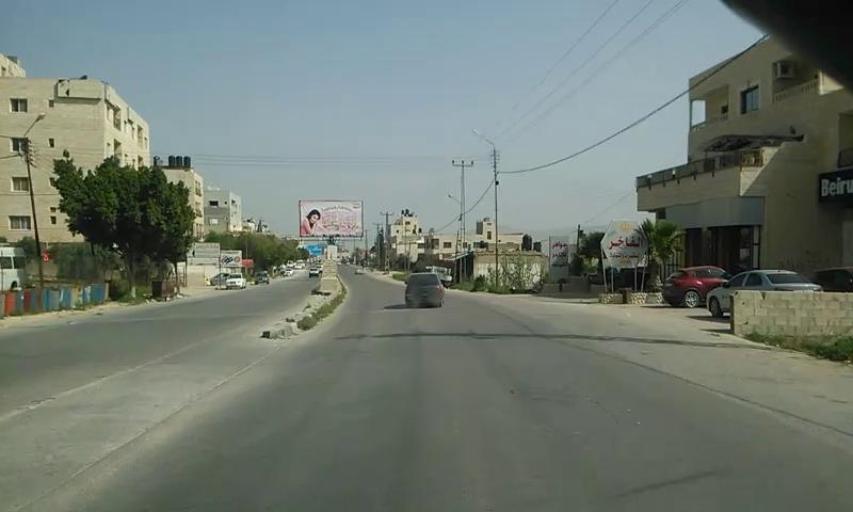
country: PS
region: West Bank
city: Kafr Qallil
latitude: 32.1915
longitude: 35.2836
